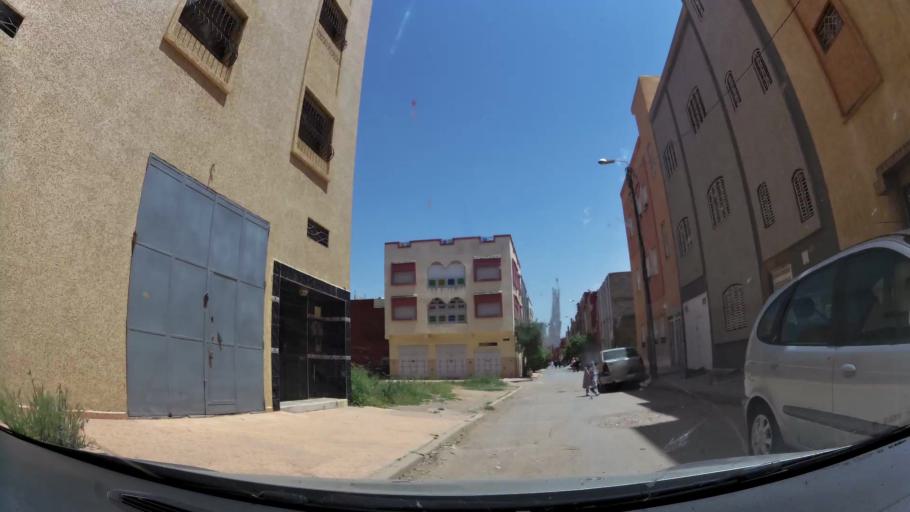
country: MA
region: Rabat-Sale-Zemmour-Zaer
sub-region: Khemisset
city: Khemisset
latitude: 33.8246
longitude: -6.0811
